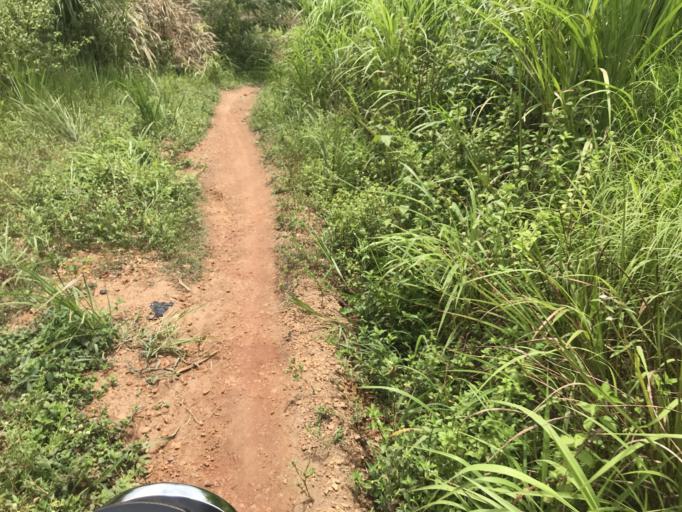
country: GN
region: Nzerekore
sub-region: Prefecture de Guekedou
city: Gueckedou
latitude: 8.4987
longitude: -10.3275
